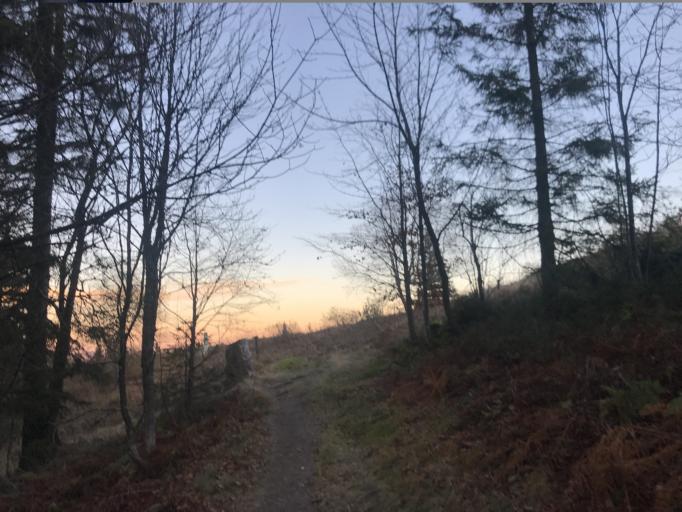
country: DE
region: Baden-Wuerttemberg
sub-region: Freiburg Region
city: Sankt Peter
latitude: 48.0633
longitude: 8.0144
